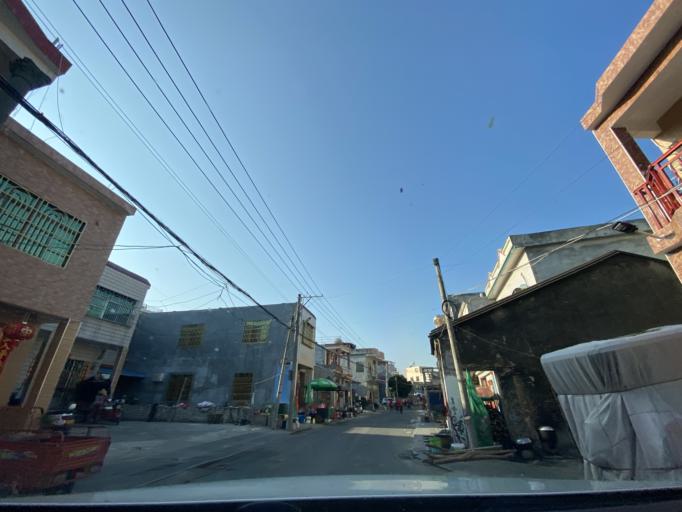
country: CN
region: Hainan
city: Yingzhou
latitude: 18.3885
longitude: 109.8187
